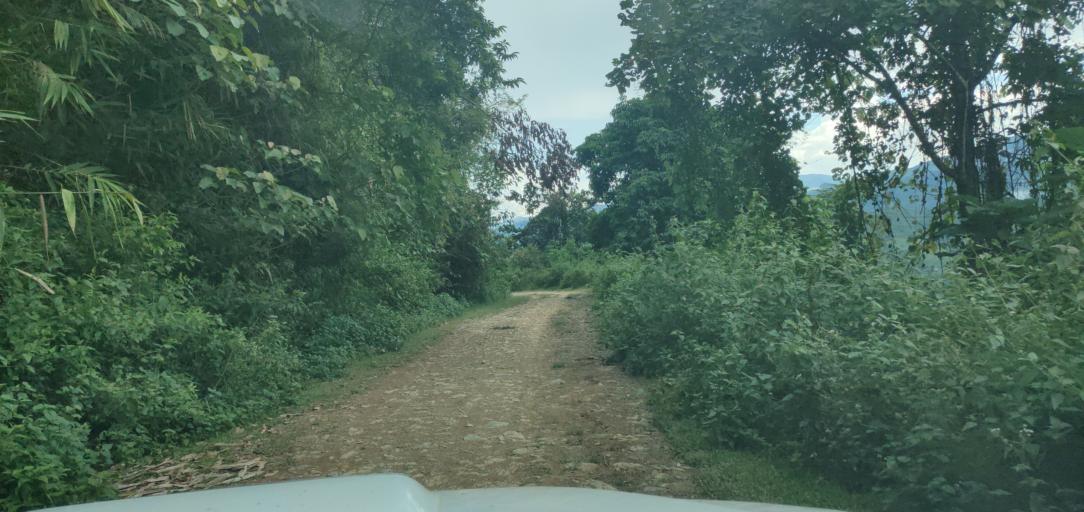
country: LA
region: Phongsali
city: Phongsali
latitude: 21.4459
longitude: 102.3155
